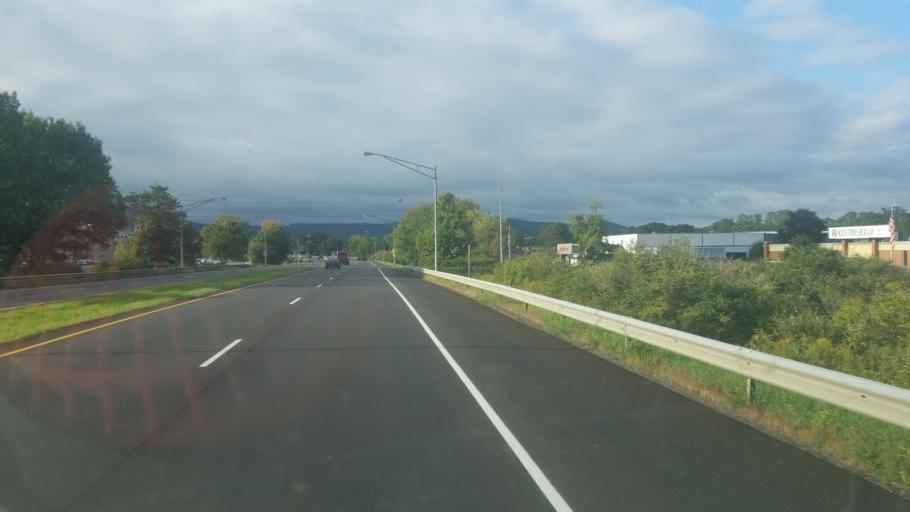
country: US
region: New York
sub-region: Cattaraugus County
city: Olean
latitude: 42.0939
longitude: -78.4283
